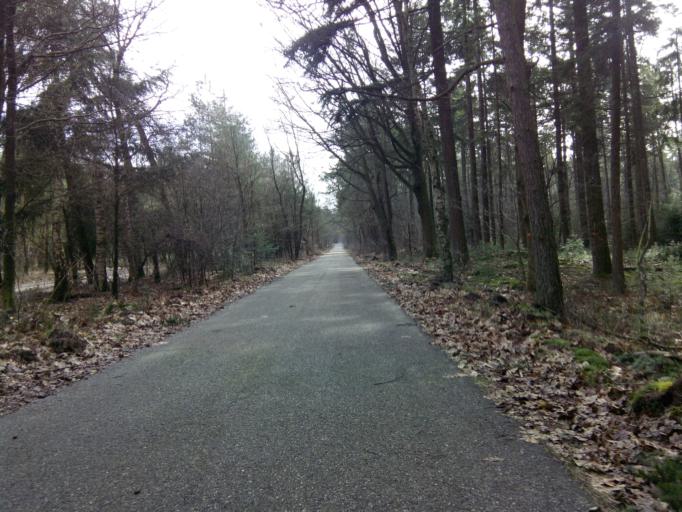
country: NL
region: Utrecht
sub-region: Gemeente Utrechtse Heuvelrug
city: Driebergen-Rijsenburg
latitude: 52.1044
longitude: 5.3175
